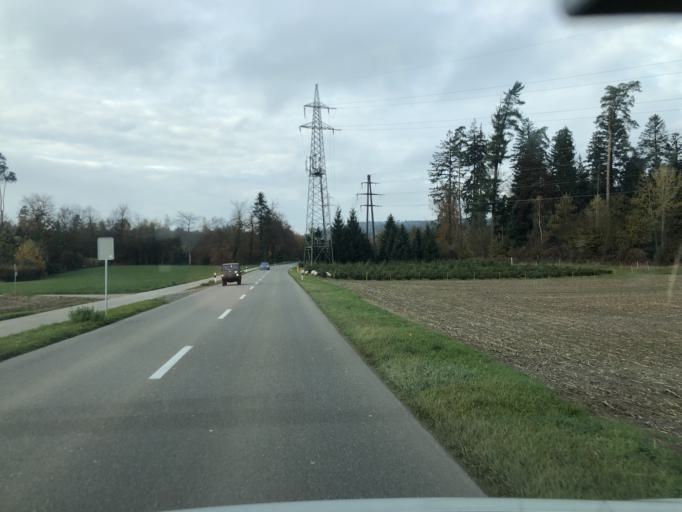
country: CH
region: Aargau
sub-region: Bezirk Baden
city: Mellingen
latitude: 47.4444
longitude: 8.2795
